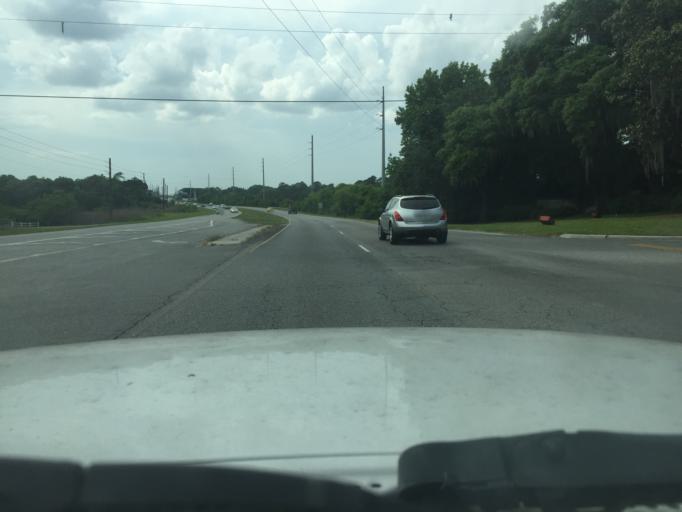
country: US
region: Georgia
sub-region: Chatham County
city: Thunderbolt
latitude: 32.0637
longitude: -81.0328
